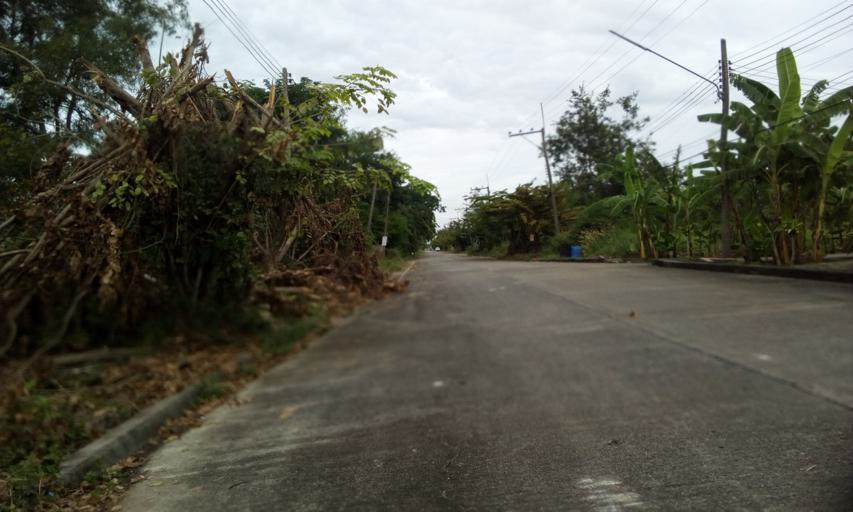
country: TH
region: Pathum Thani
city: Nong Suea
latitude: 14.0626
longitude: 100.8783
